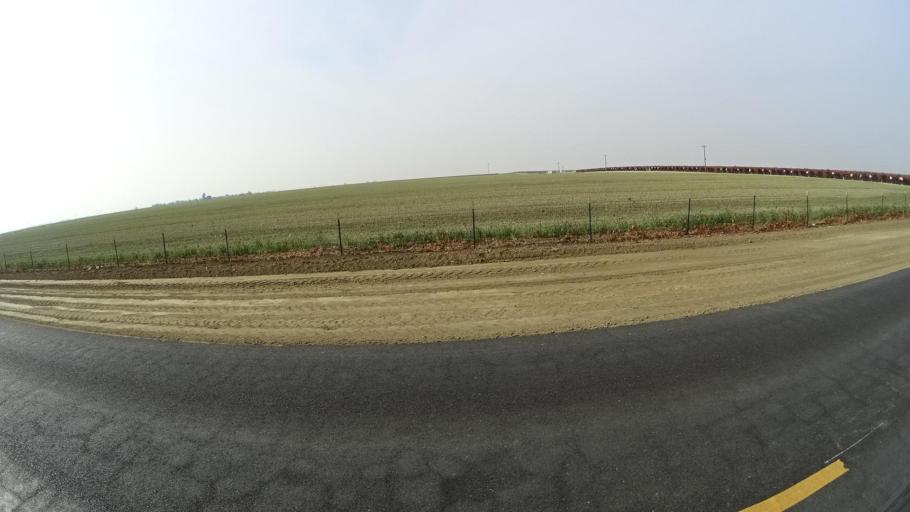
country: US
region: California
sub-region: Kern County
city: Arvin
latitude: 35.0991
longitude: -118.8505
